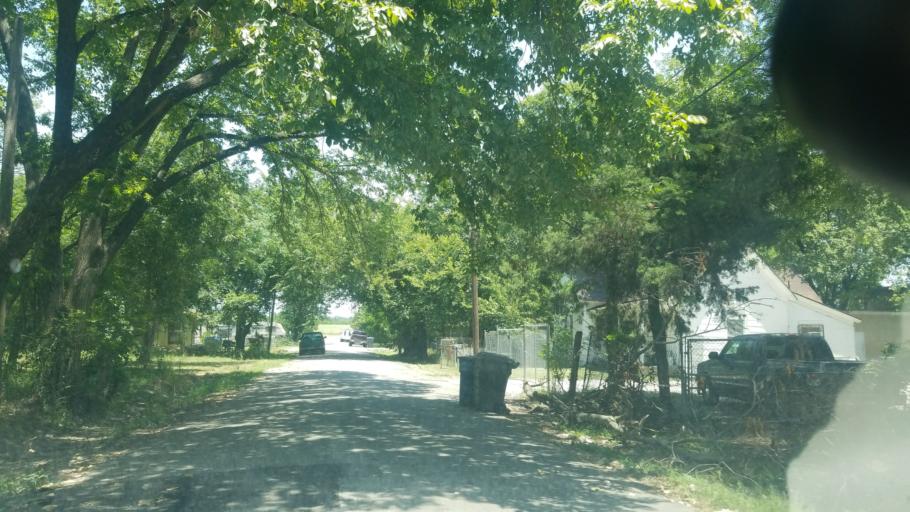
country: US
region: Texas
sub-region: Dallas County
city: Dallas
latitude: 32.7377
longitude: -96.7843
